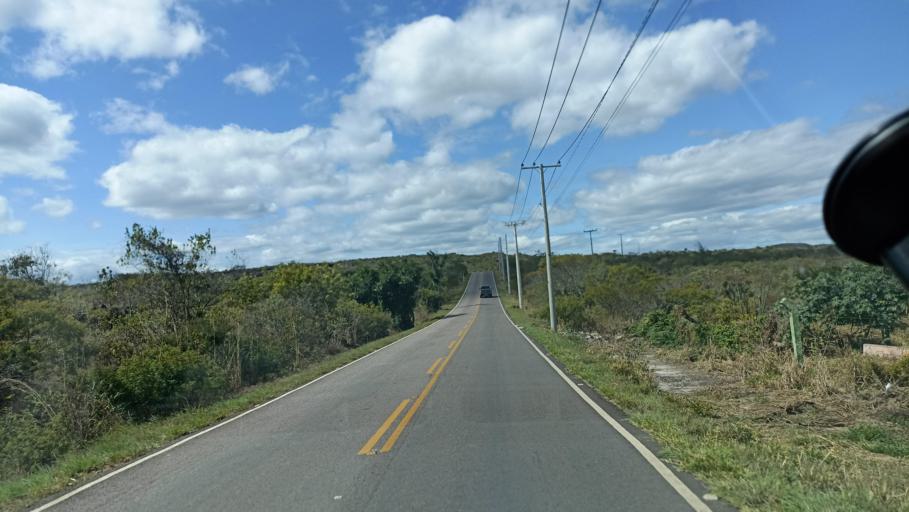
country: BR
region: Bahia
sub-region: Andarai
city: Vera Cruz
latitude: -12.9998
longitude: -41.3631
